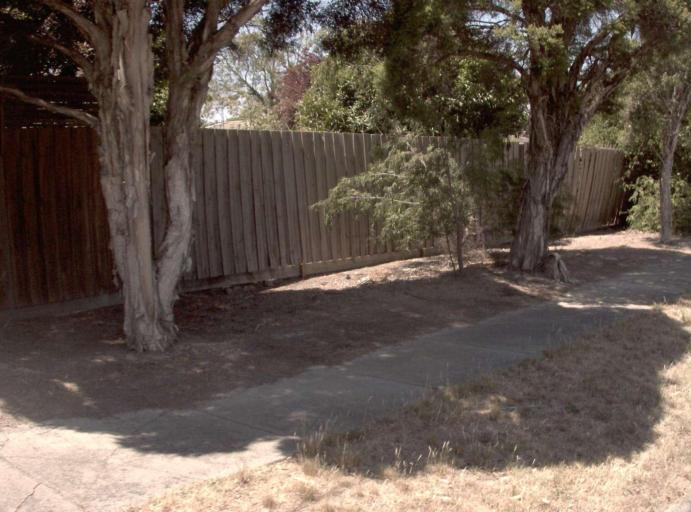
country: AU
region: Victoria
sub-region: Manningham
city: Donvale
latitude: -37.7999
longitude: 145.1785
